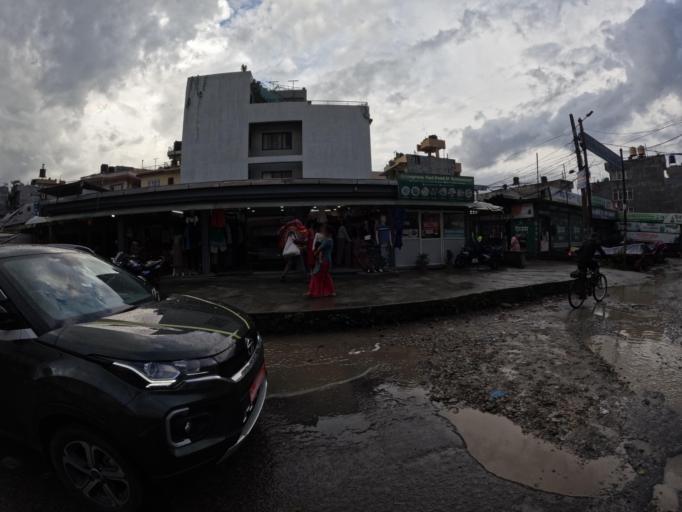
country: NP
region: Central Region
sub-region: Bagmati Zone
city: Kathmandu
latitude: 27.7513
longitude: 85.3257
